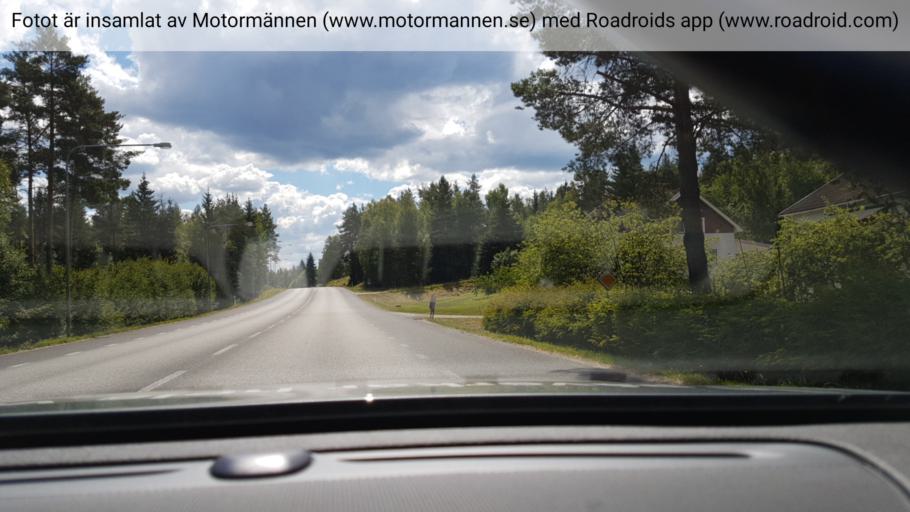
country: SE
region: Dalarna
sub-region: Faluns Kommun
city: Bjursas
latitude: 60.7321
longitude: 15.4401
